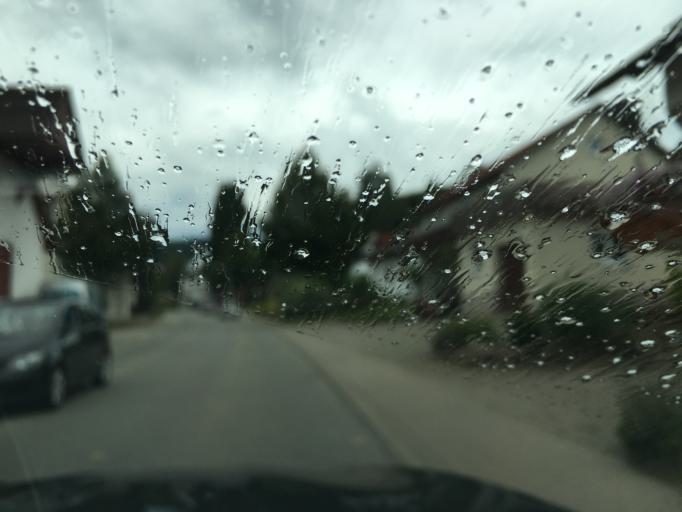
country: DE
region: Baden-Wuerttemberg
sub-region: Tuebingen Region
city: Rot
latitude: 47.8623
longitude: 9.0979
